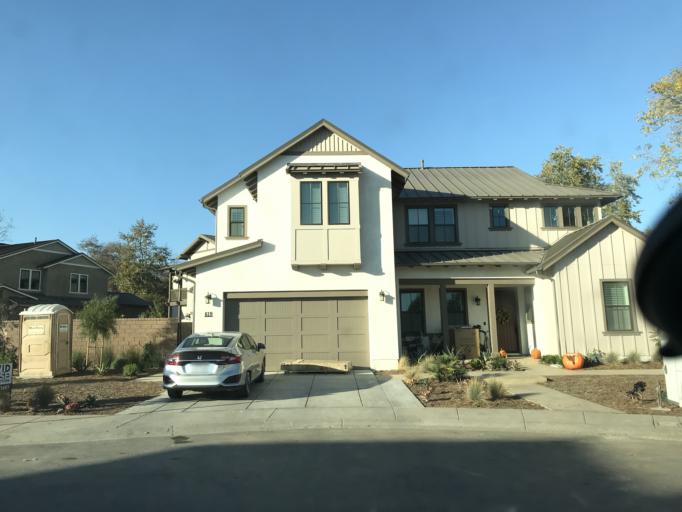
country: US
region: California
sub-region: Santa Barbara County
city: Goleta
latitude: 34.4508
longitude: -119.8127
